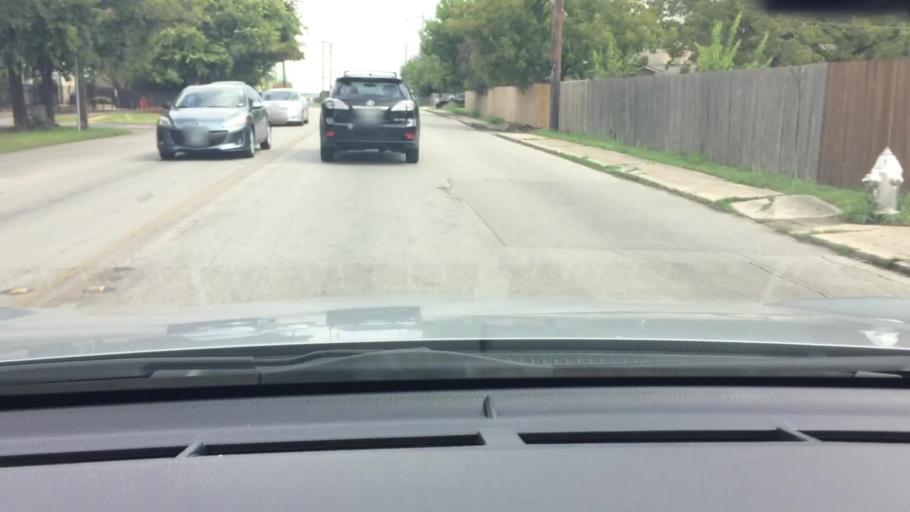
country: US
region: Texas
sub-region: Bexar County
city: Castle Hills
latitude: 29.5443
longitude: -98.5322
